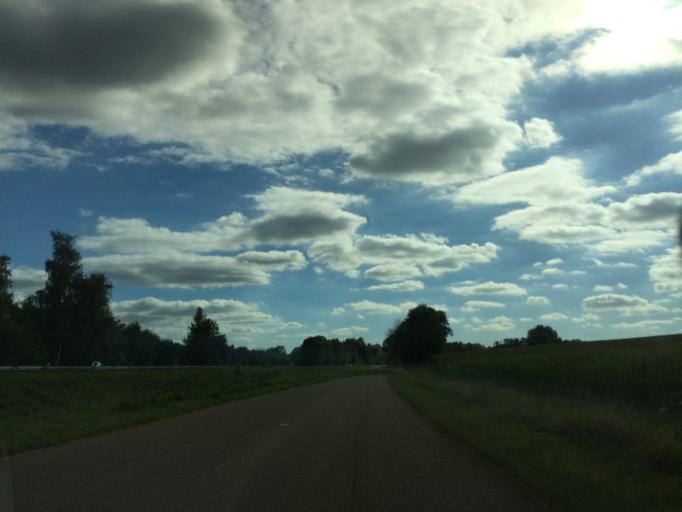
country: FR
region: Alsace
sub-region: Departement du Bas-Rhin
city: Betschdorf
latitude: 48.9368
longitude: 7.9463
